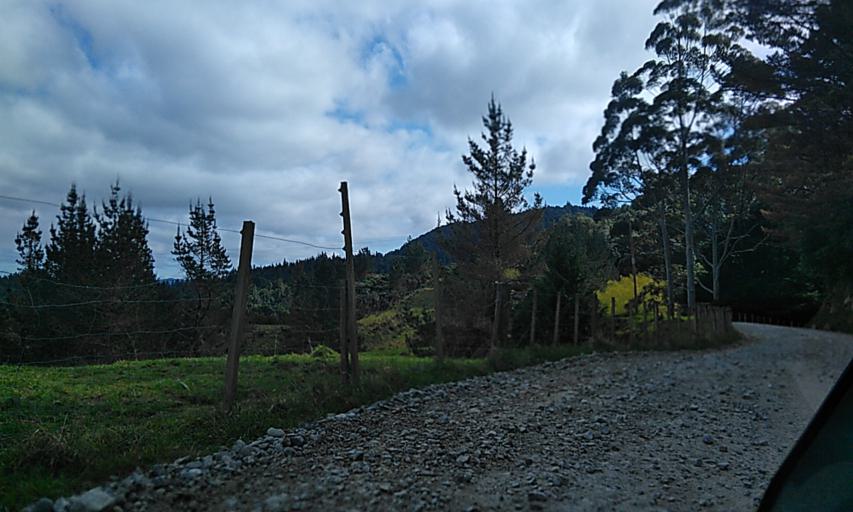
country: NZ
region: Gisborne
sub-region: Gisborne District
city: Gisborne
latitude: -38.3179
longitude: 178.0861
